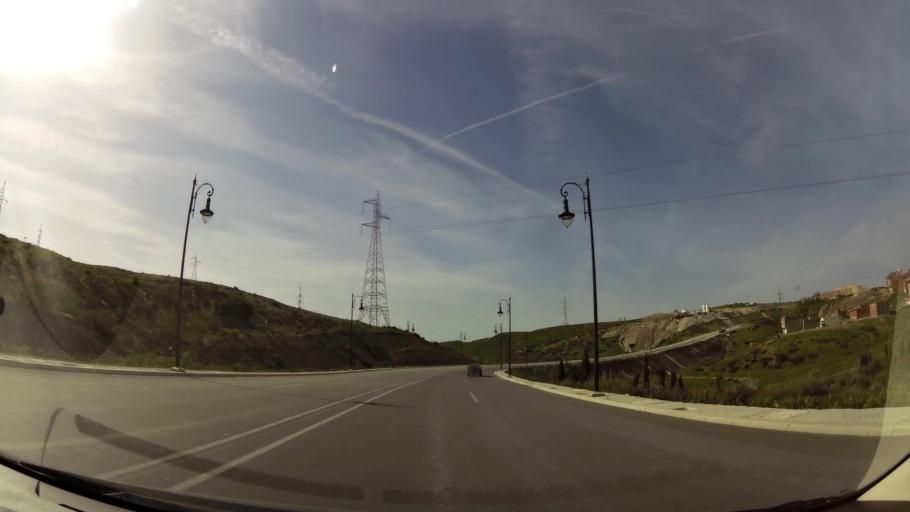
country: MA
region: Tanger-Tetouan
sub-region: Tanger-Assilah
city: Tangier
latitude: 35.7205
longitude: -5.7670
